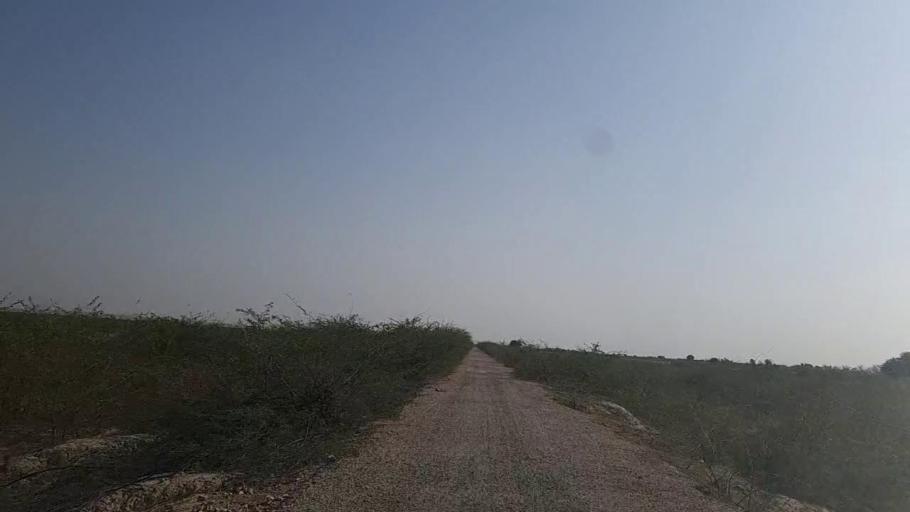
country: PK
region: Sindh
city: Kadhan
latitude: 24.5917
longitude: 69.2627
